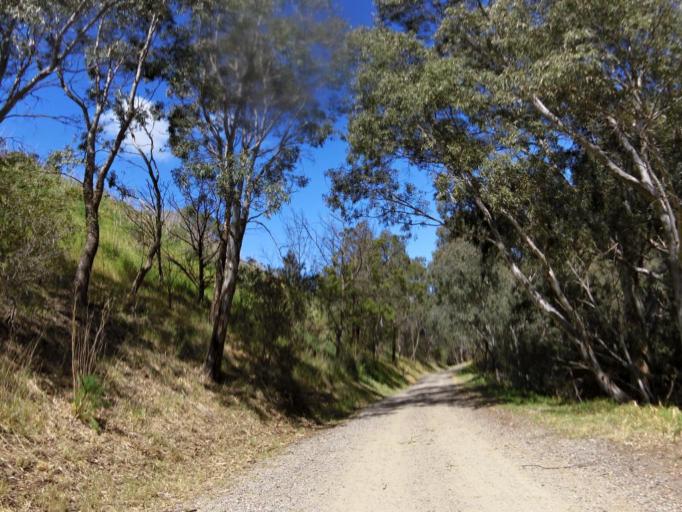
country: AU
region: Victoria
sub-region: Brimbank
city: Albion
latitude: -37.7566
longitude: 144.8495
